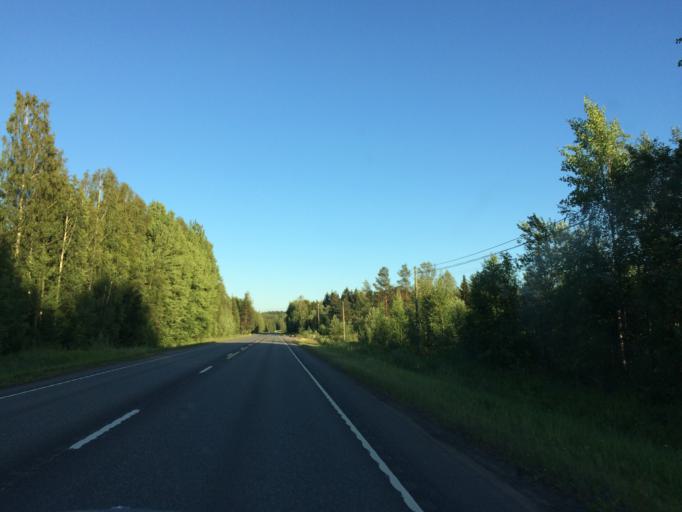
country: FI
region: Haeme
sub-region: Haemeenlinna
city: Tervakoski
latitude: 60.7768
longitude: 24.6953
